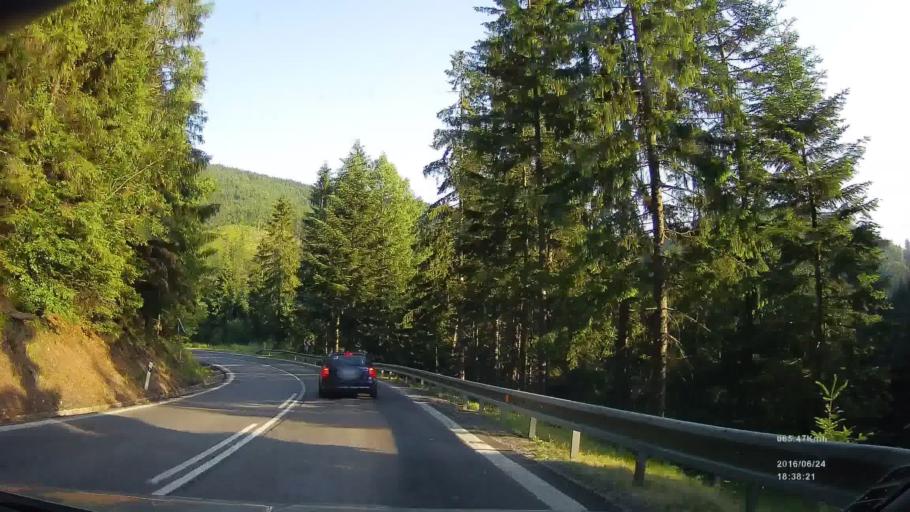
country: SK
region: Banskobystricky
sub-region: Okres Banska Bystrica
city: Brezno
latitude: 48.8945
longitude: 19.7015
